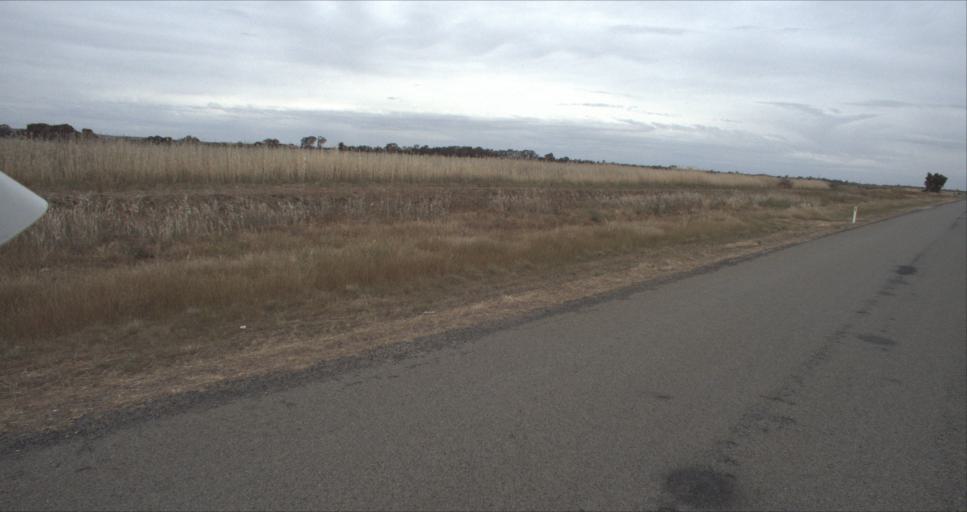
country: AU
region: New South Wales
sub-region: Leeton
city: Leeton
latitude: -34.4925
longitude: 146.4012
